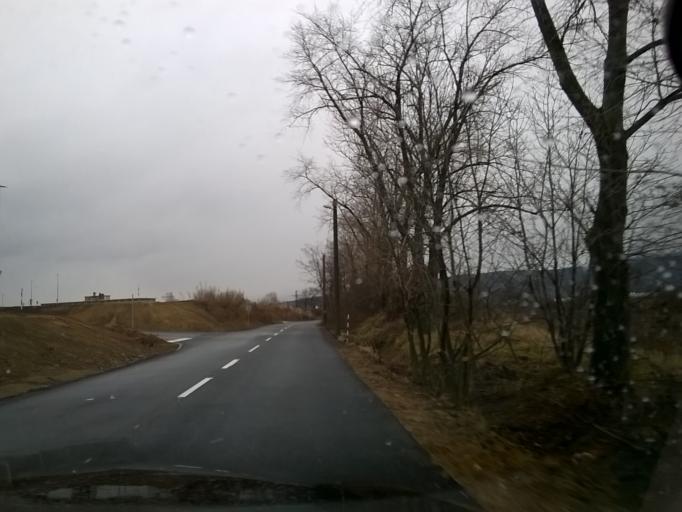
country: SK
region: Nitriansky
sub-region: Okres Nitra
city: Nitra
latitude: 48.3371
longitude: 18.0252
